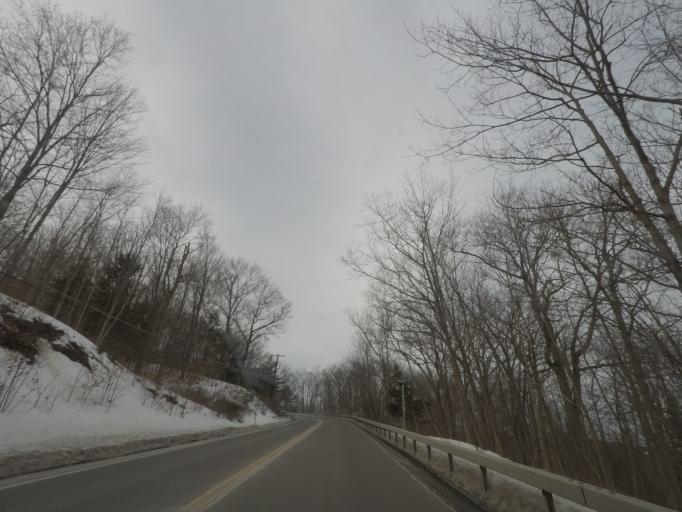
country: US
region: New York
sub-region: Albany County
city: Altamont
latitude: 42.7023
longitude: -74.0366
